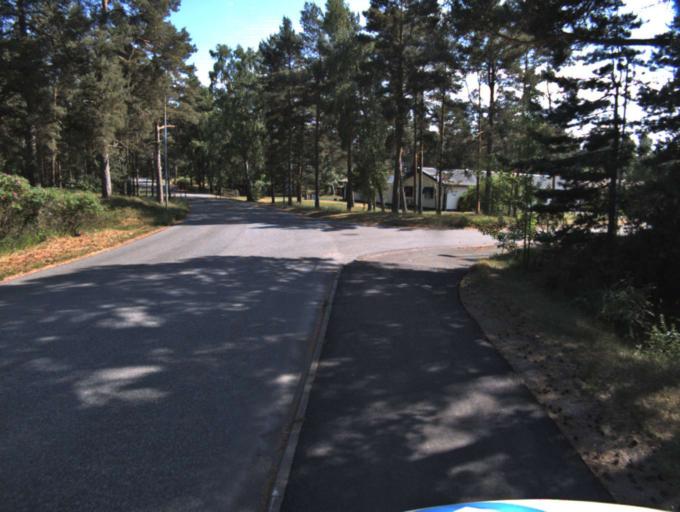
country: SE
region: Skane
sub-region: Kristianstads Kommun
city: Ahus
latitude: 55.9137
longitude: 14.2855
